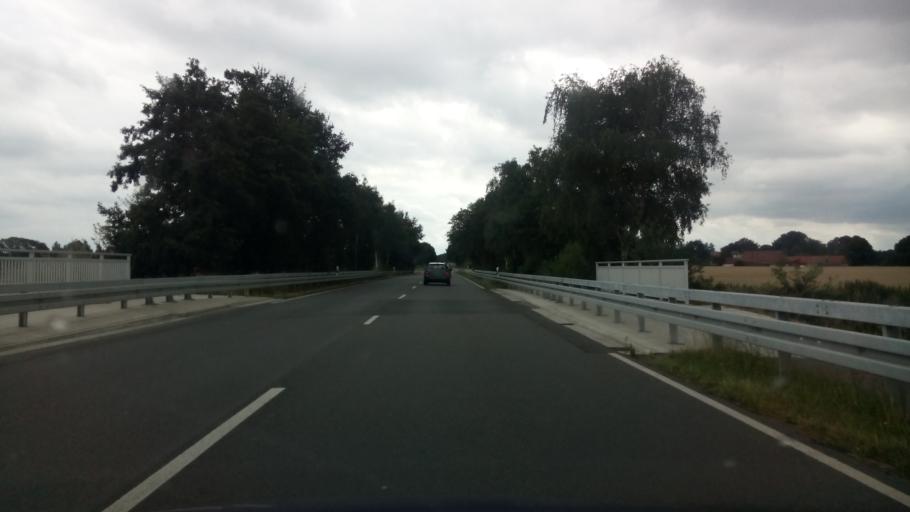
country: DE
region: Lower Saxony
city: Lembruch
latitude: 52.5275
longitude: 8.3760
